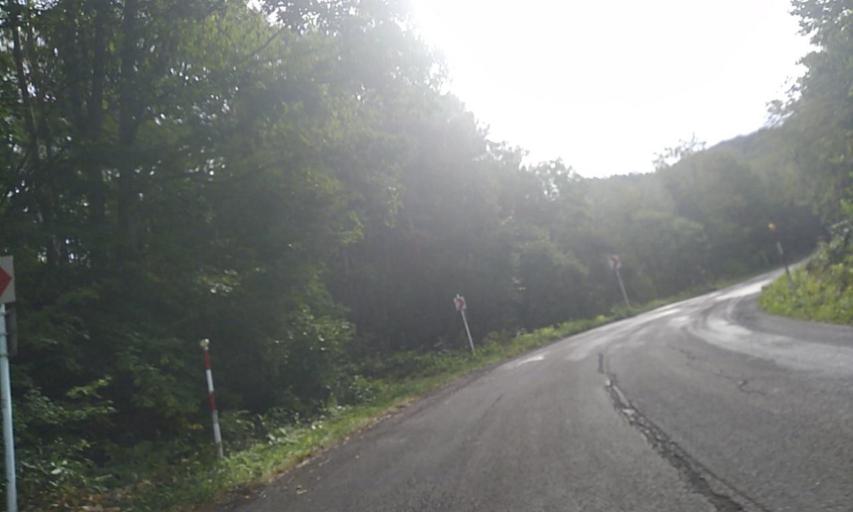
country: JP
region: Hokkaido
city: Abashiri
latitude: 43.6790
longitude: 144.5461
